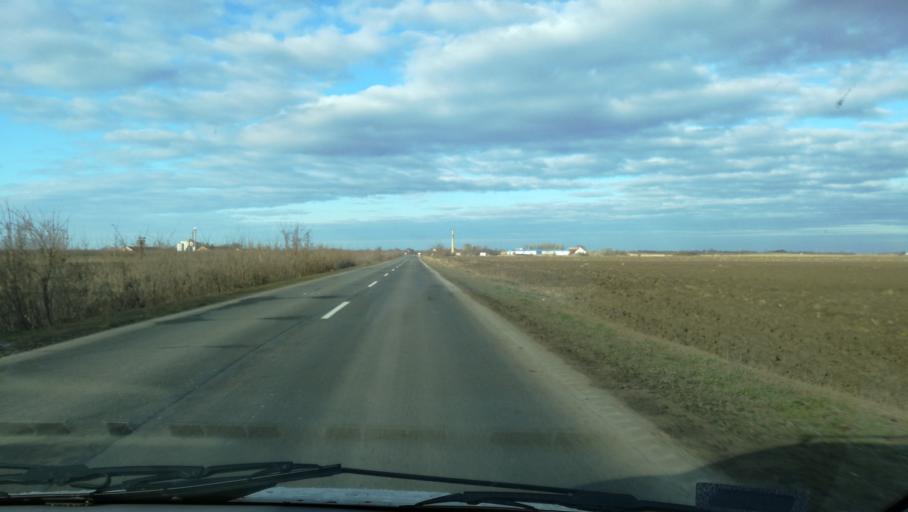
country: RS
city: Tiszahegyes
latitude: 45.8225
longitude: 20.3453
